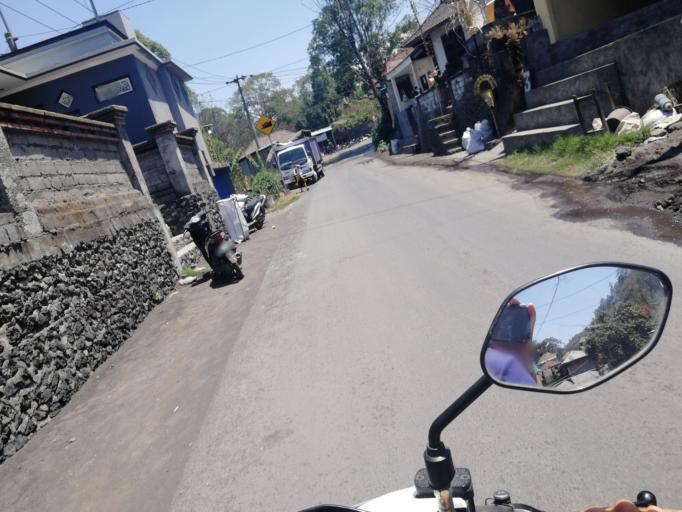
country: ID
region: Bali
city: Banjar Trunyan
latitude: -8.2288
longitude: 115.4093
